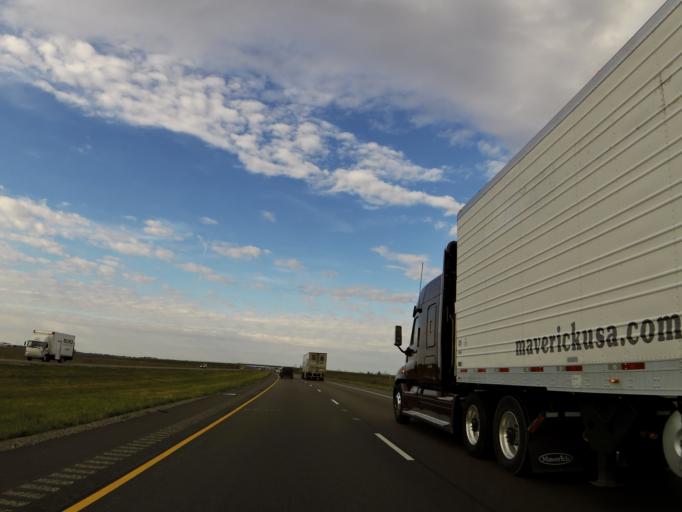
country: US
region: Illinois
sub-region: Washington County
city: Okawville
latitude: 38.4276
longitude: -89.4699
